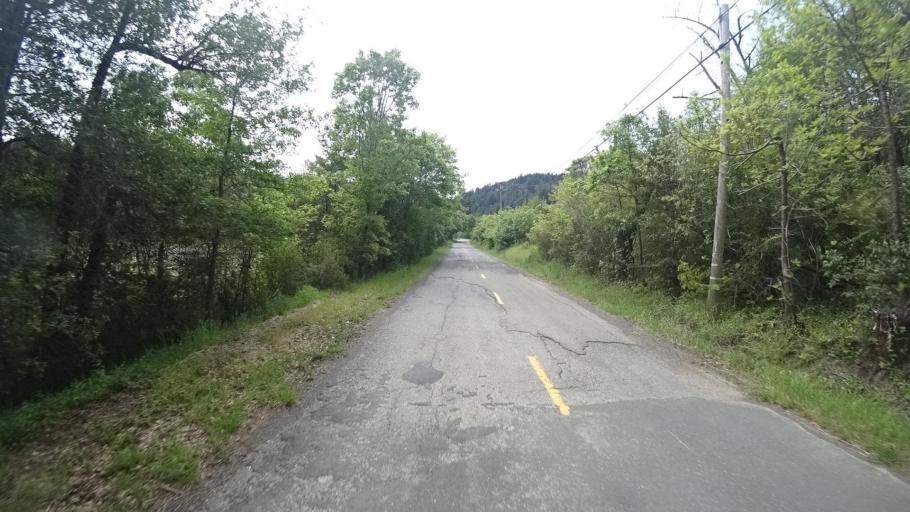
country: US
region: California
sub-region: Humboldt County
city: Redway
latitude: 40.0721
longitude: -123.8284
